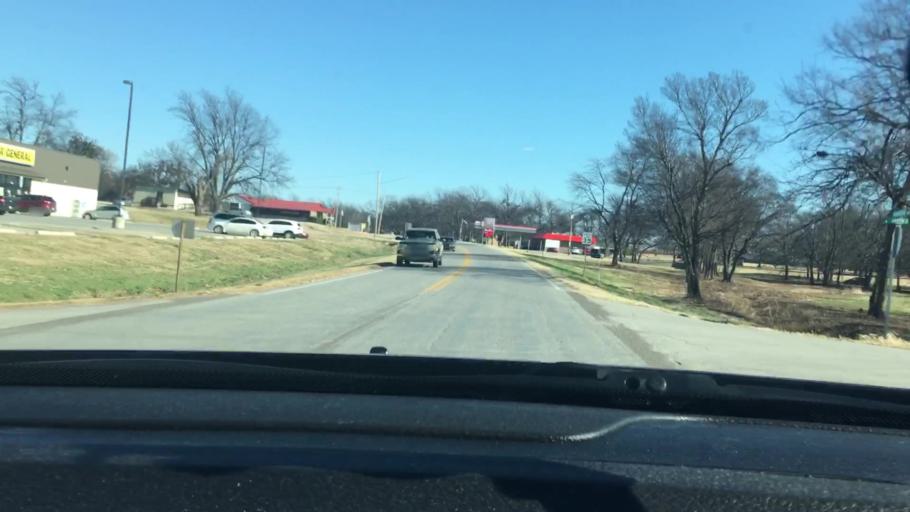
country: US
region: Oklahoma
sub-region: Garvin County
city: Wynnewood
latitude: 34.6444
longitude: -97.1580
